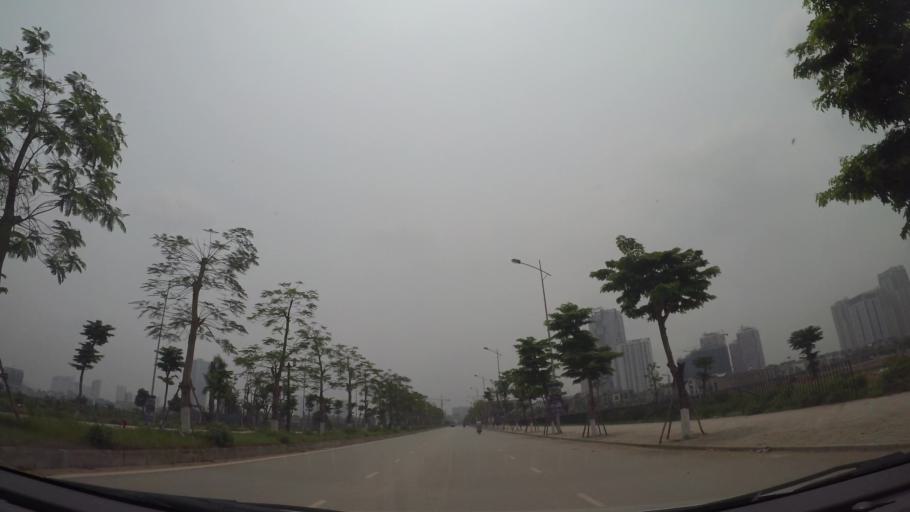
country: VN
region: Ha Noi
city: Ha Dong
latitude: 20.9817
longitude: 105.7585
